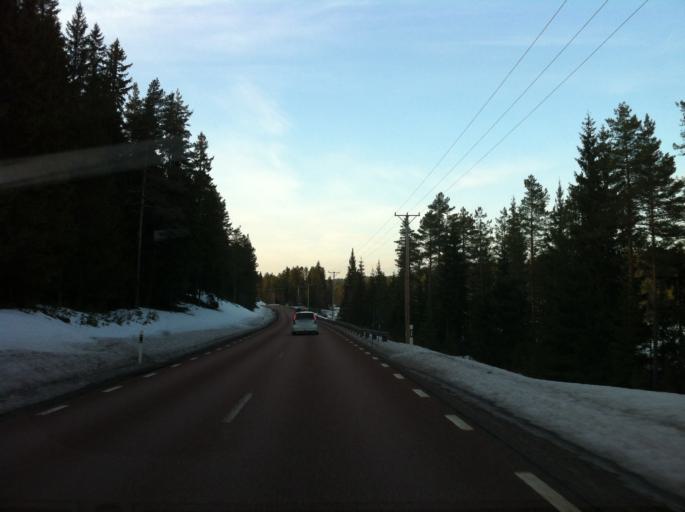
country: SE
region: Vaermland
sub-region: Filipstads Kommun
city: Lesjofors
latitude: 60.2454
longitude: 14.1800
